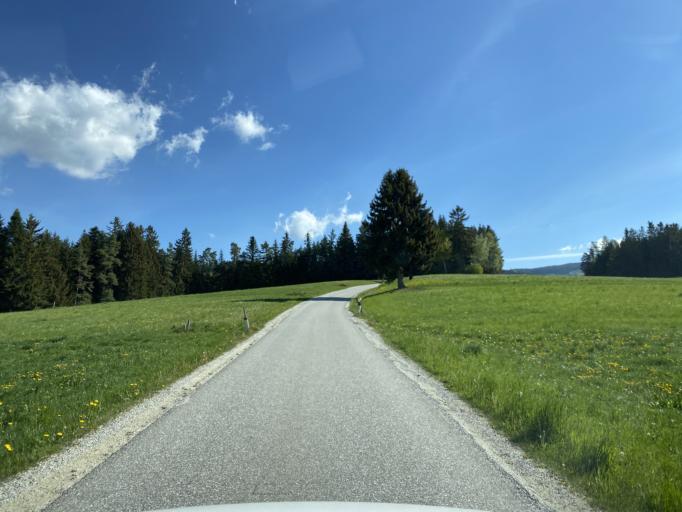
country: AT
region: Styria
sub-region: Politischer Bezirk Weiz
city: Strallegg
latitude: 47.3743
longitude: 15.7195
